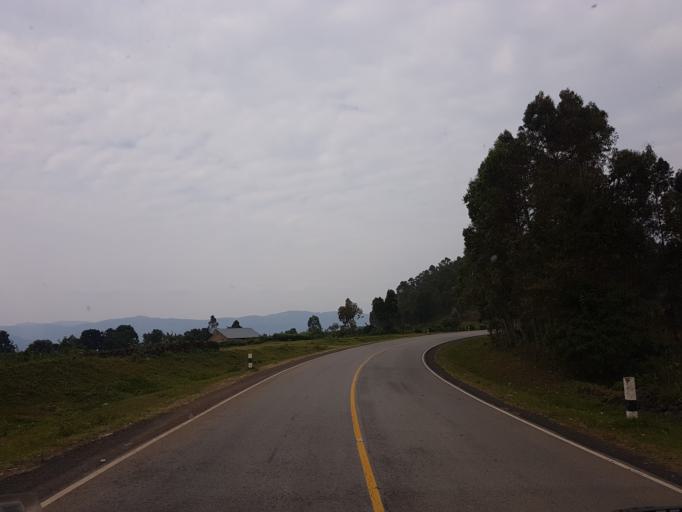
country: UG
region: Western Region
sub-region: Kisoro District
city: Kisoro
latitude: -1.3288
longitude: 29.7333
